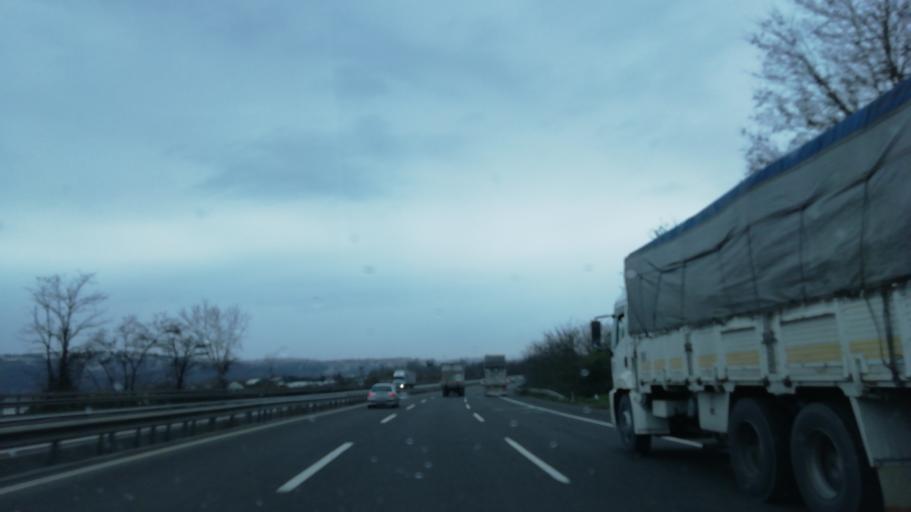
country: TR
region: Sakarya
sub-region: Merkez
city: Sapanca
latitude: 40.7098
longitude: 30.3219
